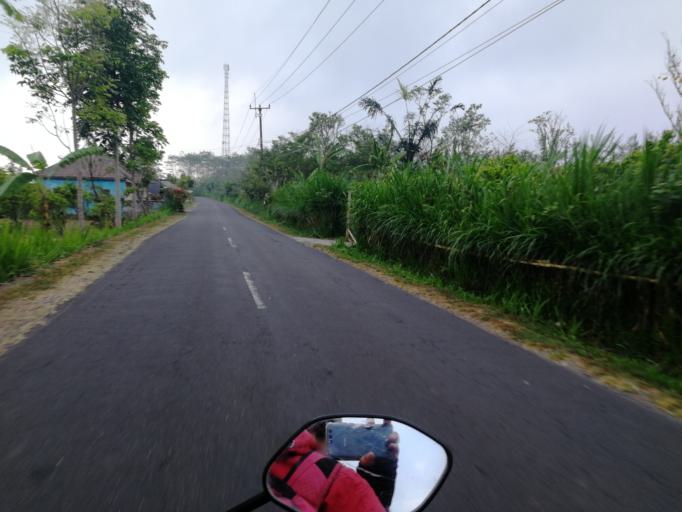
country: ID
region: Bali
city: Banjar Ambengan
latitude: -8.2398
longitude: 115.2418
